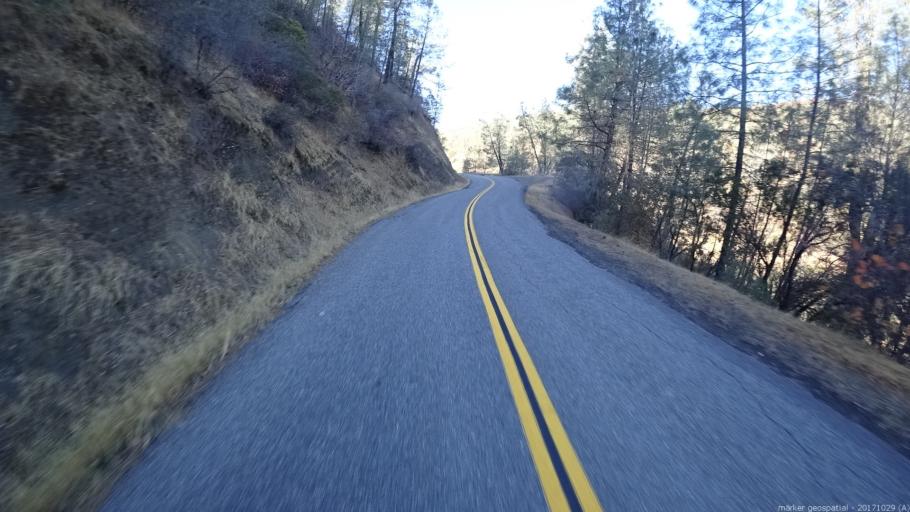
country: US
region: California
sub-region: Trinity County
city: Lewiston
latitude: 40.3860
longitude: -122.8332
